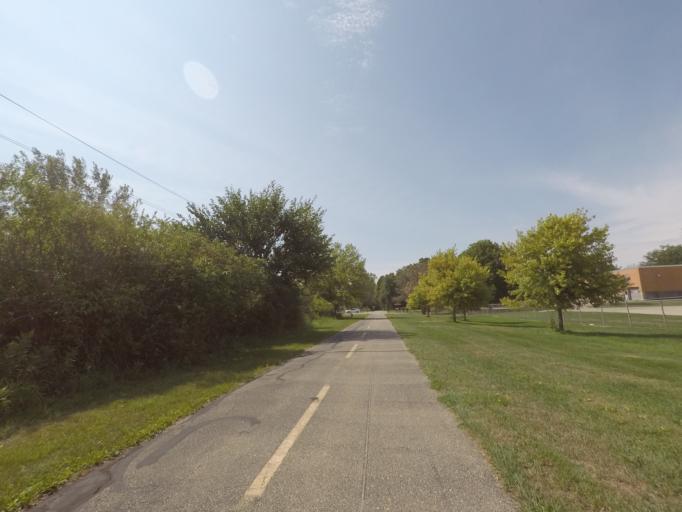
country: US
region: Wisconsin
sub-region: Jefferson County
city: Fort Atkinson
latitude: 42.9052
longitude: -88.8574
